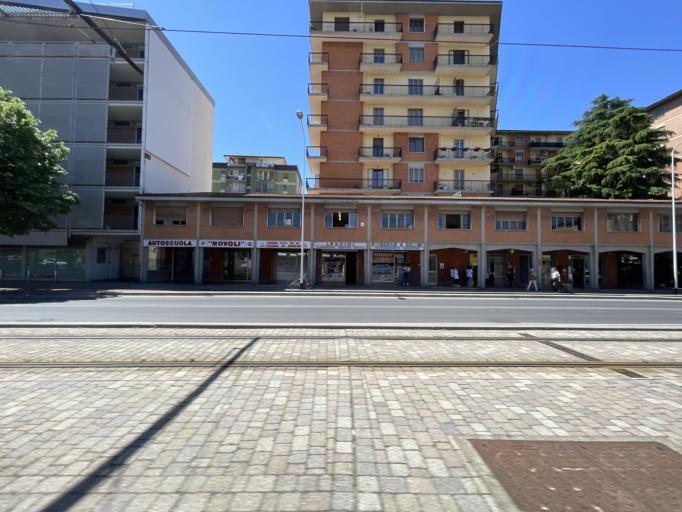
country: IT
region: Tuscany
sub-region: Province of Florence
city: Florence
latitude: 43.7939
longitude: 11.2185
